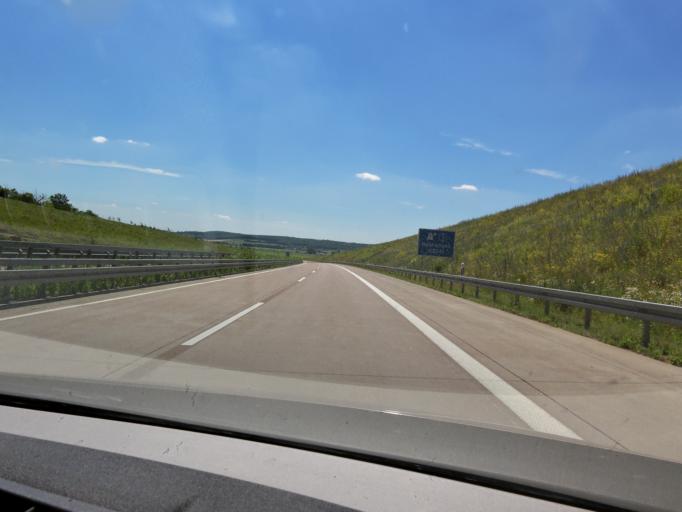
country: DE
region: Thuringia
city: Bretleben
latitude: 51.3206
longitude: 11.2404
